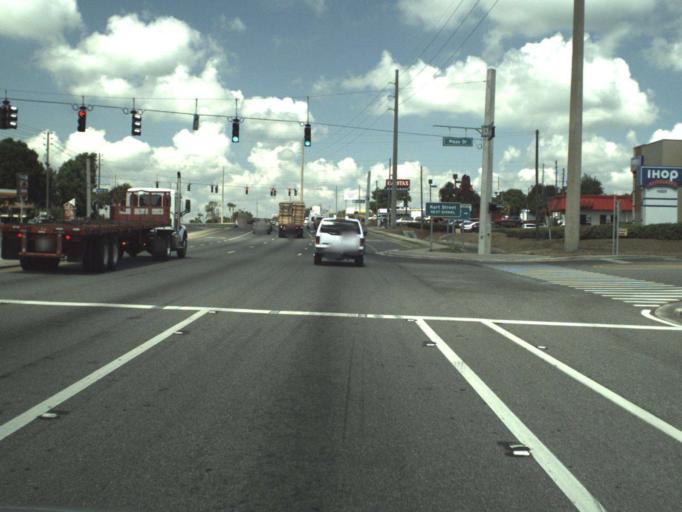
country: US
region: Florida
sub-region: Lake County
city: Eustis
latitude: 28.8234
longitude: -81.6899
